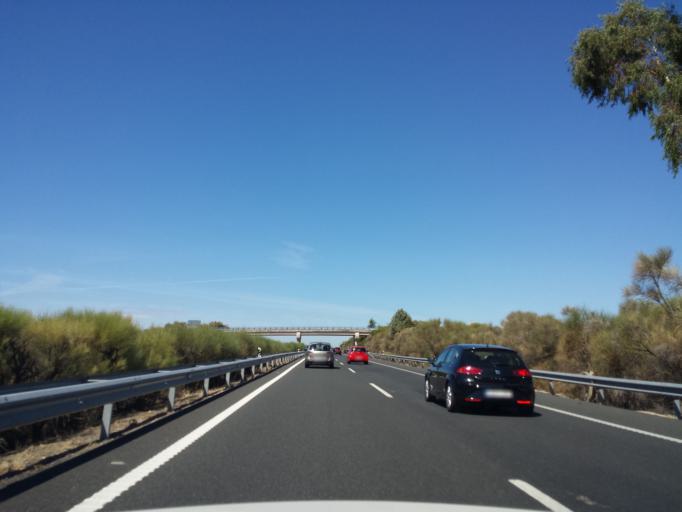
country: ES
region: Extremadura
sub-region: Provincia de Caceres
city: Peraleda de la Mata
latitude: 39.8908
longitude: -5.4274
